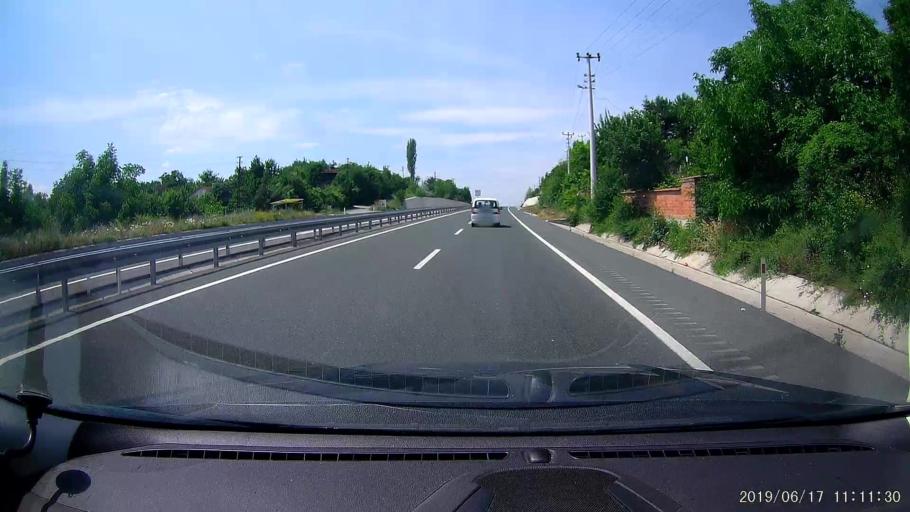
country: TR
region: Kastamonu
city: Tosya
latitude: 40.9857
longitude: 34.0084
